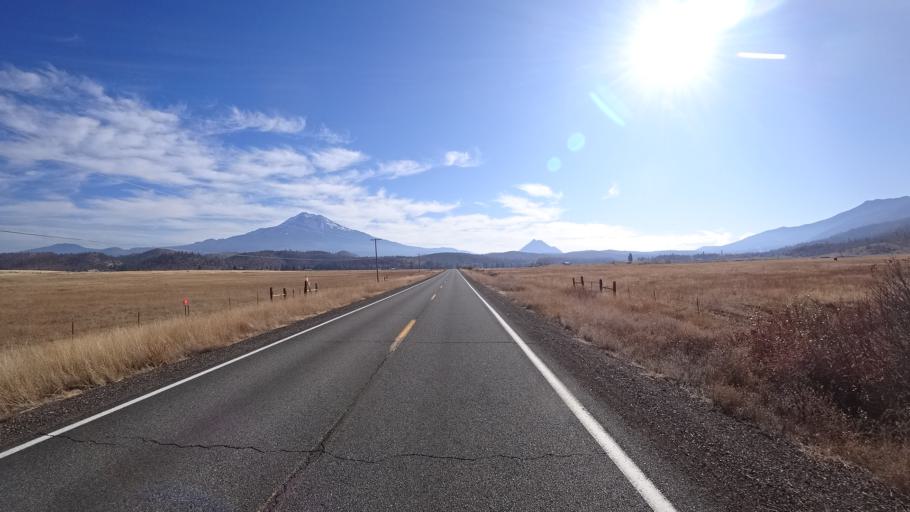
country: US
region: California
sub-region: Siskiyou County
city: Weed
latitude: 41.4474
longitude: -122.4488
